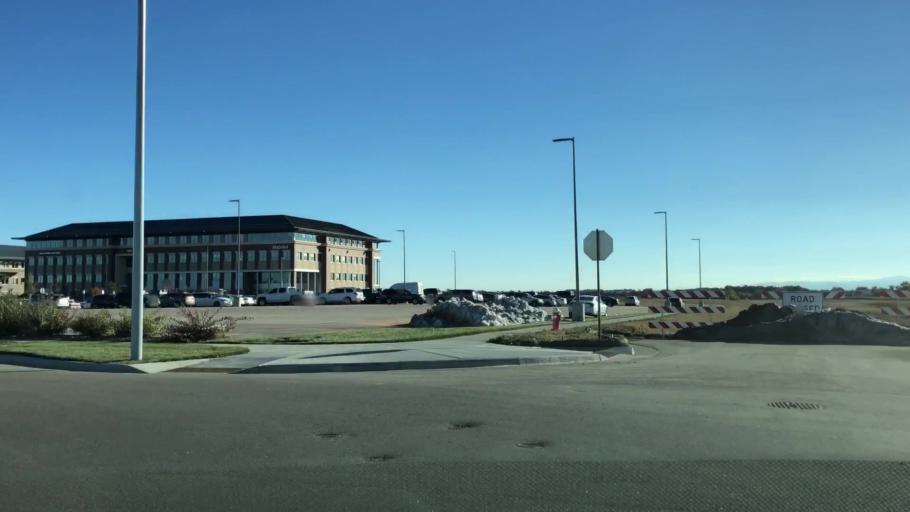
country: US
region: Colorado
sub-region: Larimer County
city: Loveland
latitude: 40.4242
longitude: -105.0048
